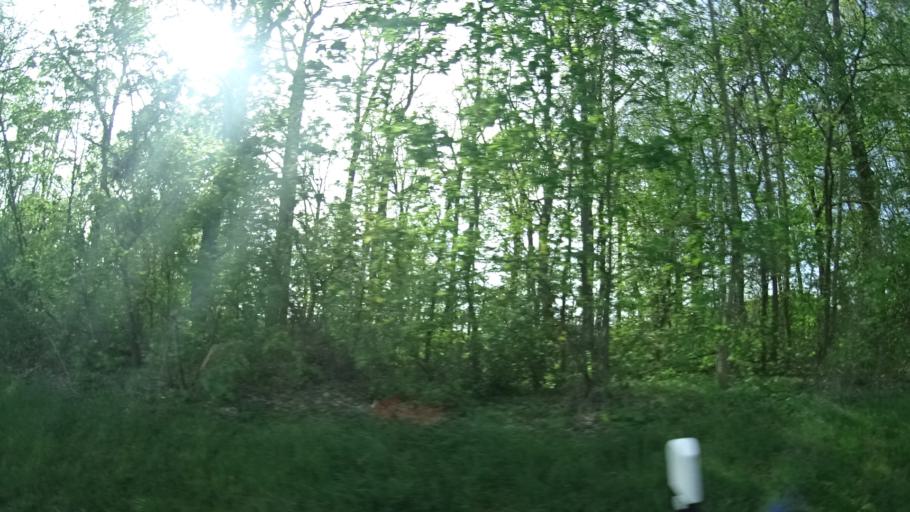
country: DE
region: Bavaria
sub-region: Regierungsbezirk Unterfranken
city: Kolitzheim
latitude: 49.8924
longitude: 10.2284
